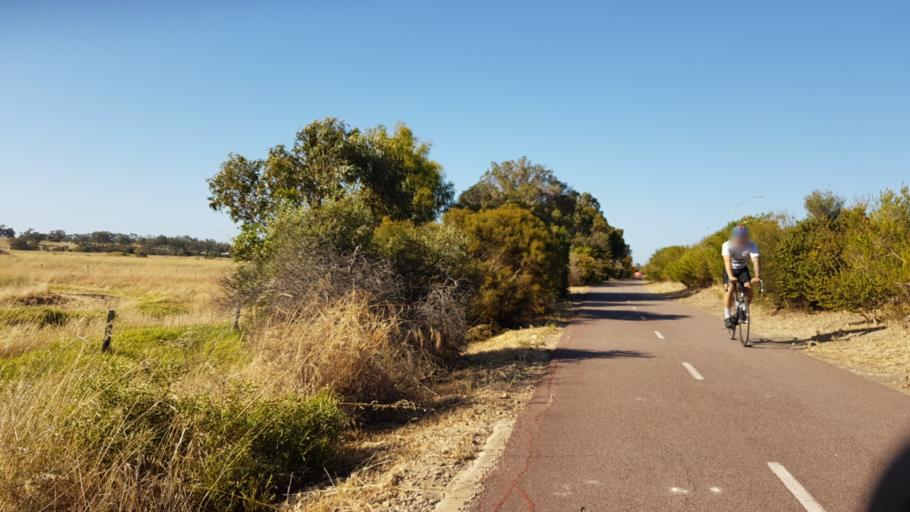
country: AU
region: Western Australia
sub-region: Kwinana
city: Wellard
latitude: -32.3018
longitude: 115.8331
